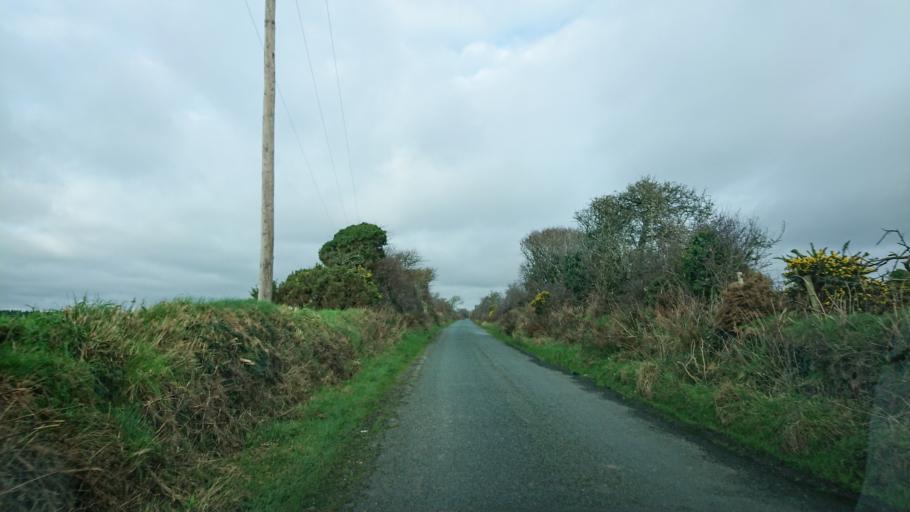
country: IE
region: Munster
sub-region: Waterford
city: Portlaw
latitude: 52.1566
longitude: -7.3085
